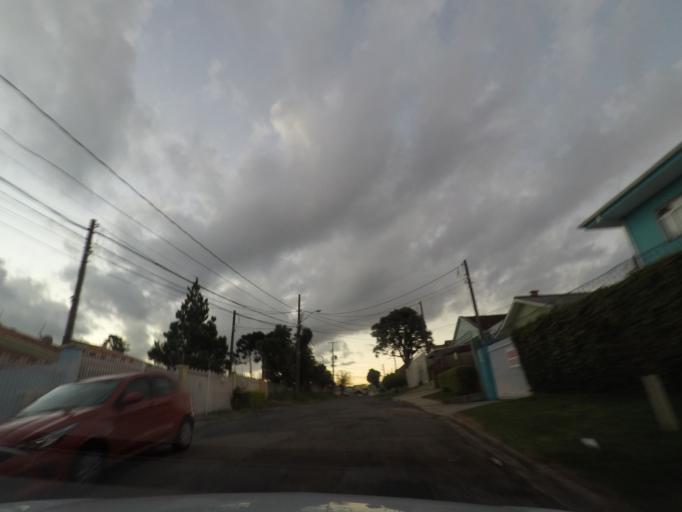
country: BR
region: Parana
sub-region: Sao Jose Dos Pinhais
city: Sao Jose dos Pinhais
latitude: -25.4976
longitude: -49.2653
